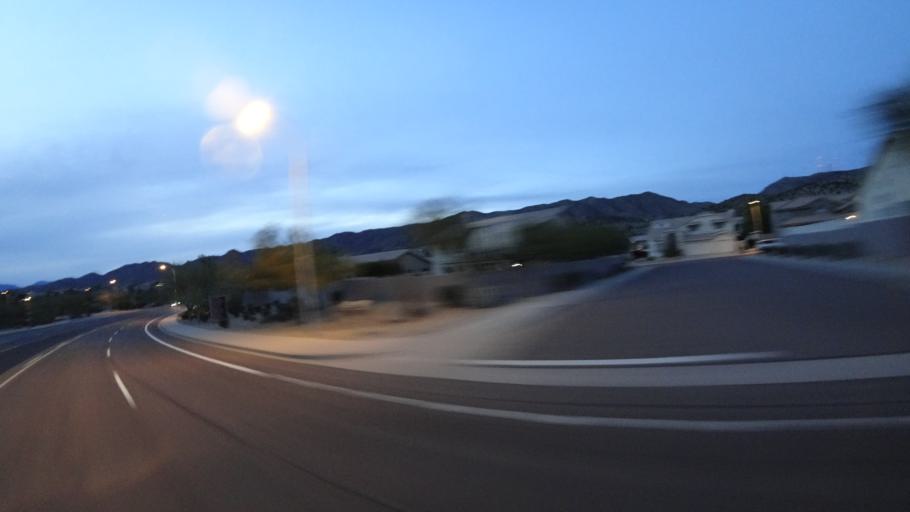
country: US
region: Arizona
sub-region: Maricopa County
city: Laveen
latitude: 33.3039
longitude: -112.0744
